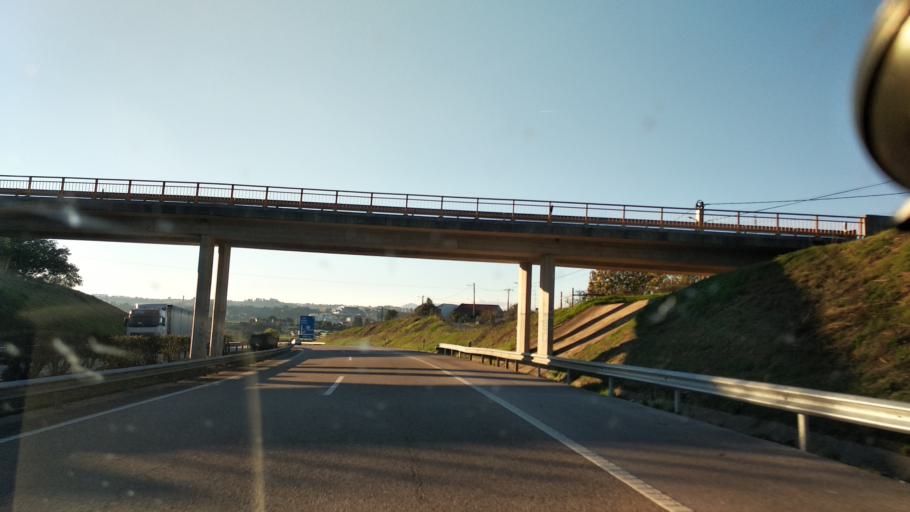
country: PT
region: Santarem
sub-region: Torres Novas
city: Riachos
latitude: 39.4693
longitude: -8.5140
